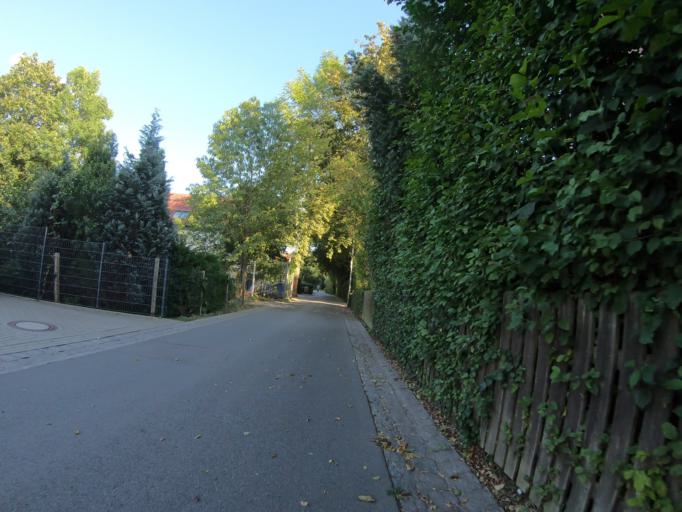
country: DE
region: Lower Saxony
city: Gifhorn
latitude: 52.4871
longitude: 10.5436
